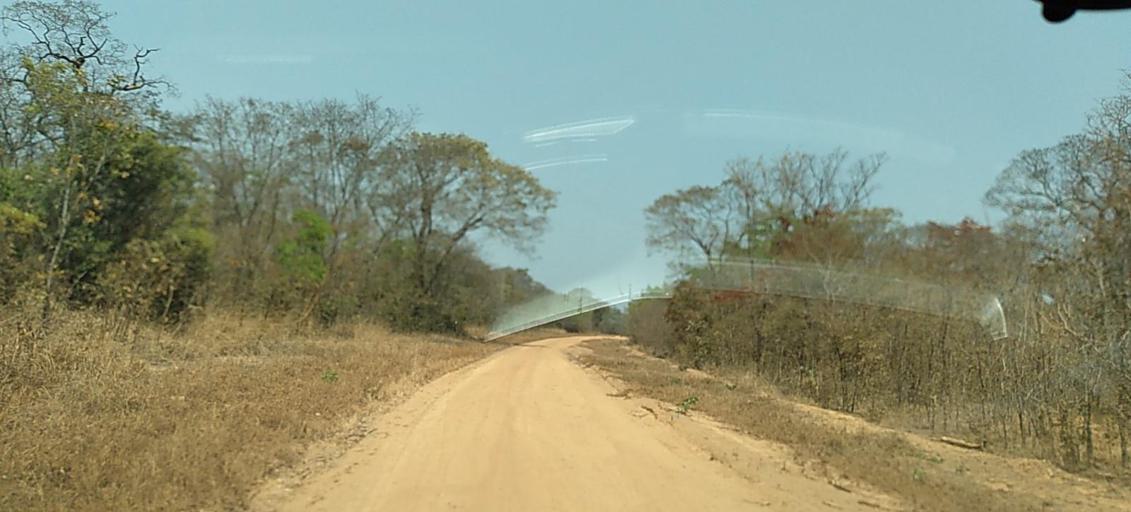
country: ZM
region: Central
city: Mumbwa
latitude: -14.3550
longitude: 26.4789
